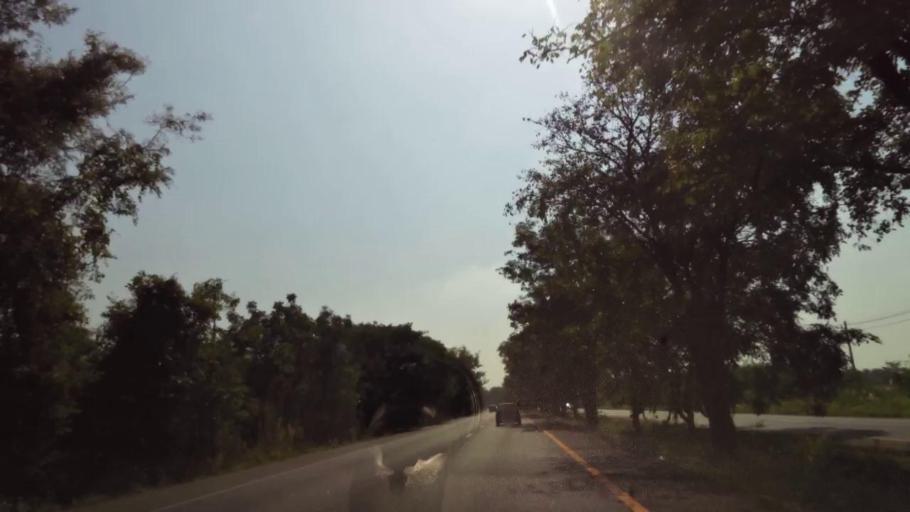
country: TH
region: Phichit
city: Bueng Na Rang
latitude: 16.0305
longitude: 100.1154
